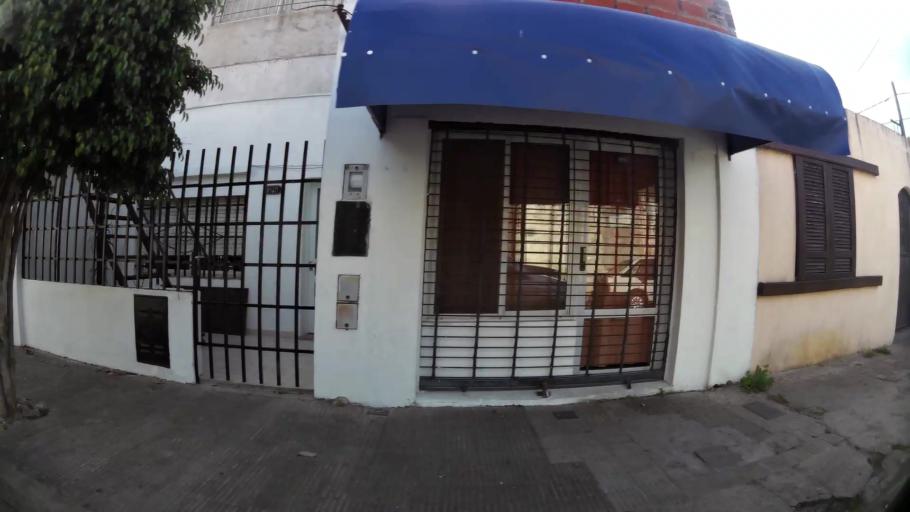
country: AR
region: Santa Fe
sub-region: Departamento de Rosario
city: Rosario
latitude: -32.9206
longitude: -60.6891
